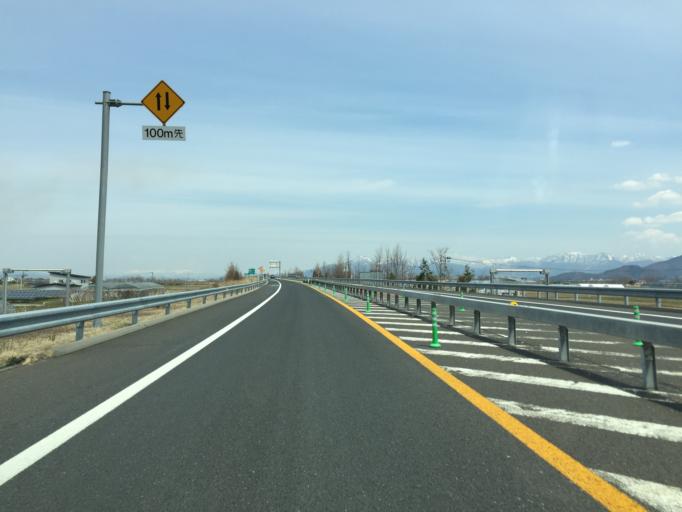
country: JP
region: Yamagata
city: Tendo
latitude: 38.3195
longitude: 140.3244
